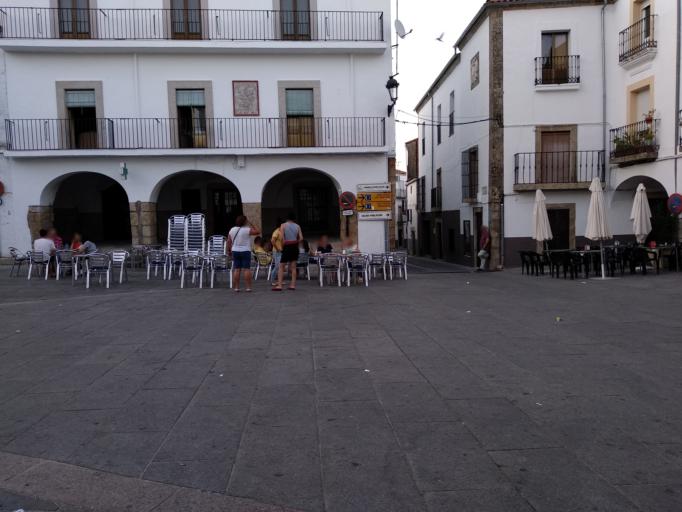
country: ES
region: Extremadura
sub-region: Provincia de Caceres
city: Montanchez
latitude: 39.2251
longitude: -6.1525
